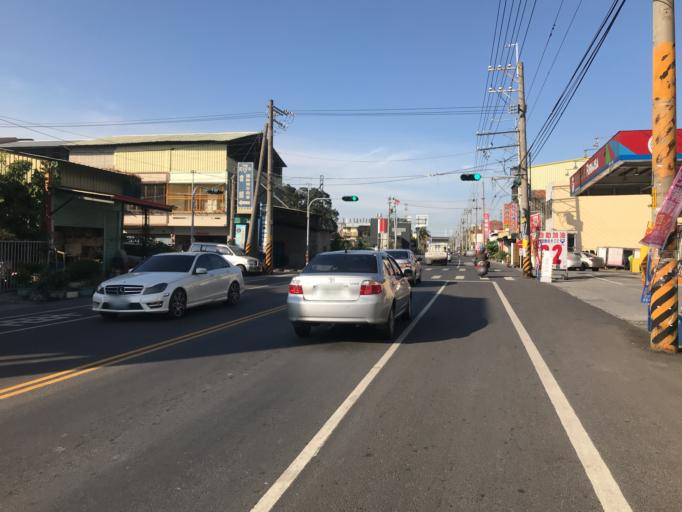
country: TW
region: Taiwan
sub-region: Nantou
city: Nantou
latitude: 23.8758
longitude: 120.5873
